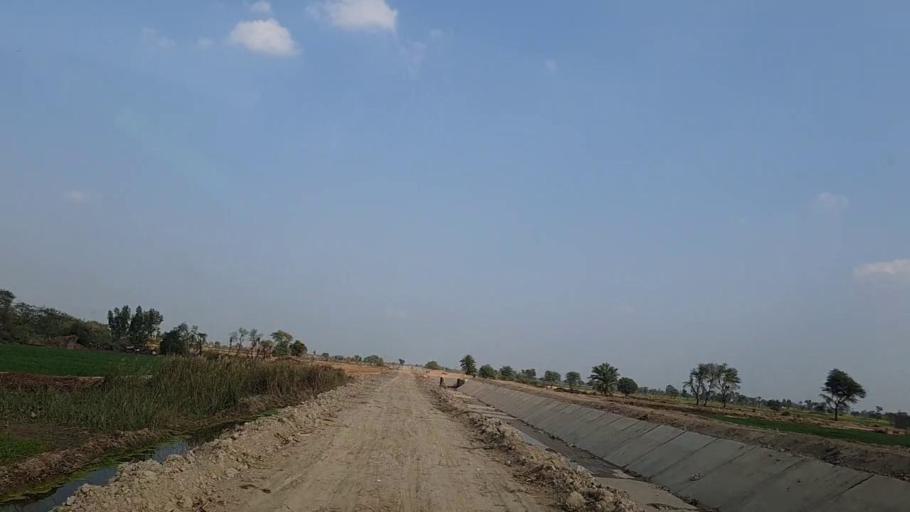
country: PK
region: Sindh
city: Nawabshah
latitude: 26.1484
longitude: 68.3819
